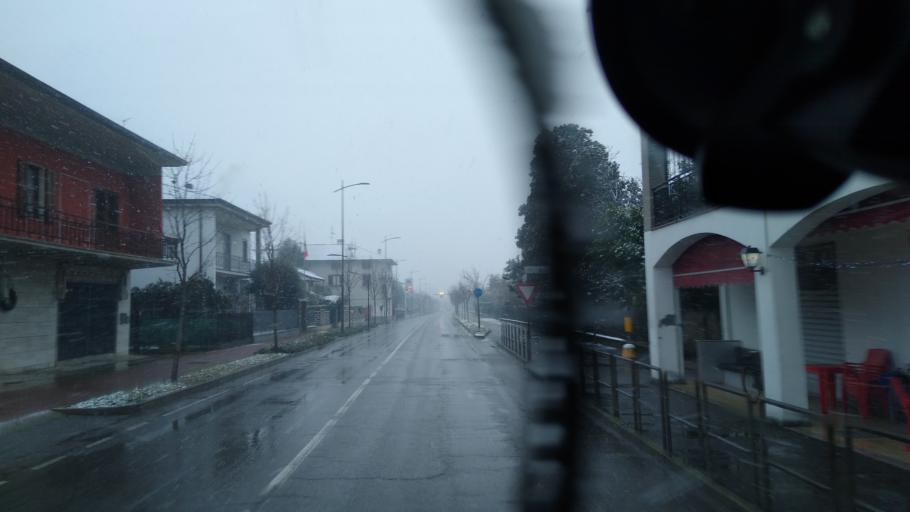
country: IT
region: Lombardy
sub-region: Provincia di Bergamo
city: Morengo
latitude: 45.5327
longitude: 9.7051
